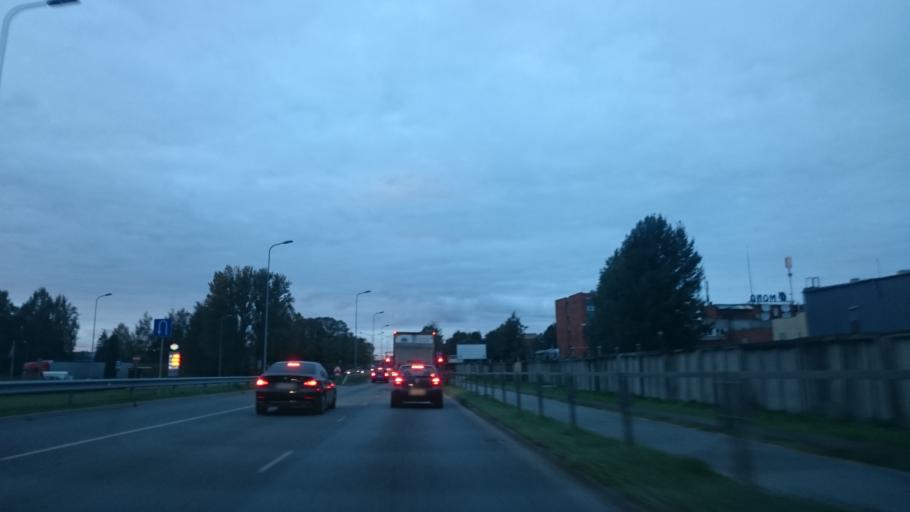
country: LV
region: Kekava
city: Balozi
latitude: 56.9245
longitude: 24.1891
